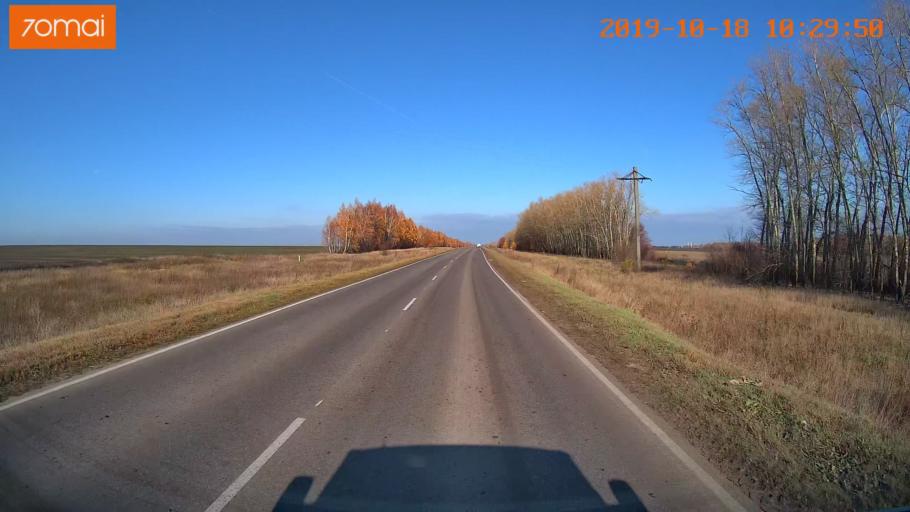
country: RU
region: Tula
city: Kurkino
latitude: 53.4567
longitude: 38.6513
